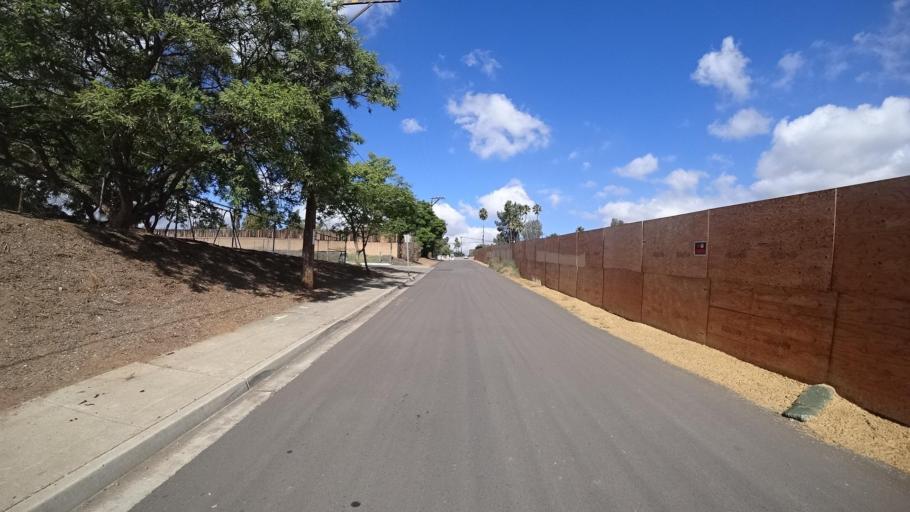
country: US
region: California
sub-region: San Diego County
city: Rancho San Diego
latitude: 32.7613
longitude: -116.9451
